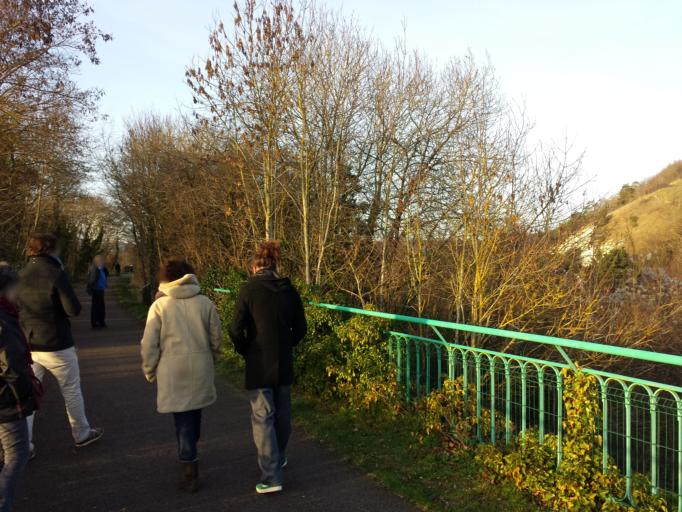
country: FR
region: Haute-Normandie
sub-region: Departement de l'Eure
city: Evreux
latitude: 49.0232
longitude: 1.1244
